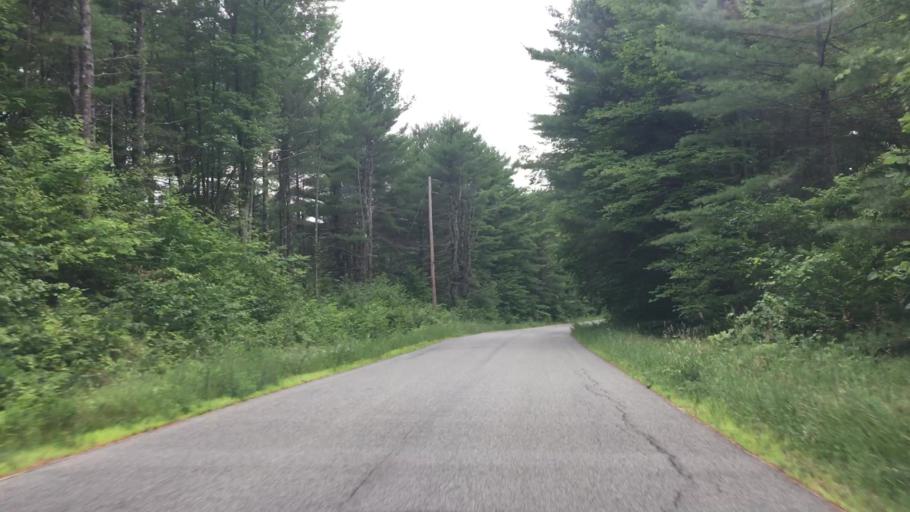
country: US
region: New York
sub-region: Essex County
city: Keeseville
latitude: 44.4455
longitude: -73.6043
